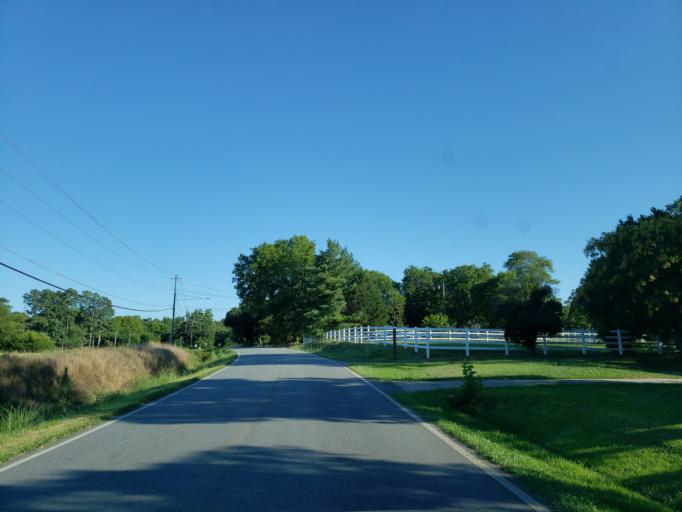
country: US
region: Georgia
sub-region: Bartow County
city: Euharlee
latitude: 34.0907
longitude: -84.9906
